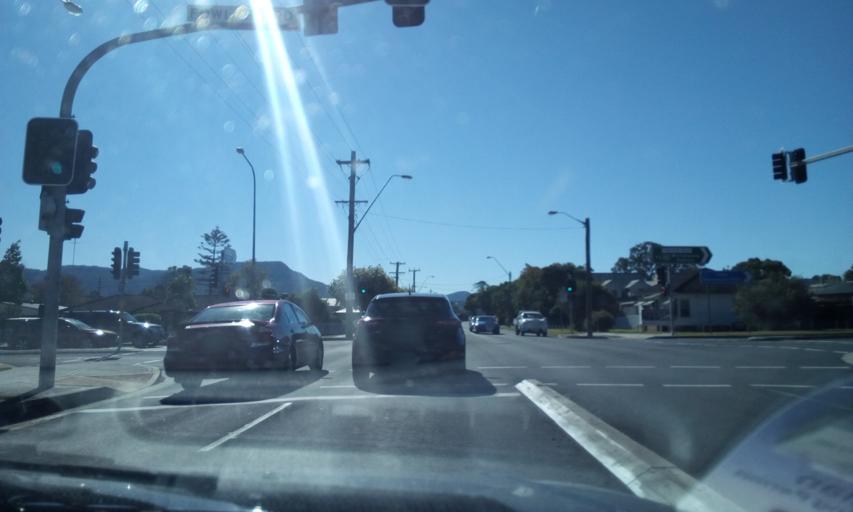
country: AU
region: New South Wales
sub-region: Wollongong
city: Dapto
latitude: -34.4985
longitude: 150.7911
